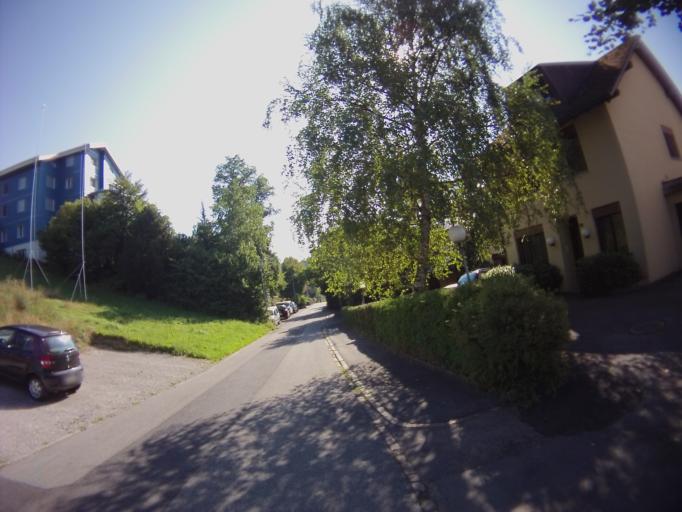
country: CH
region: Zug
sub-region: Zug
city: Unterageri
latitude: 47.1373
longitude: 8.5980
